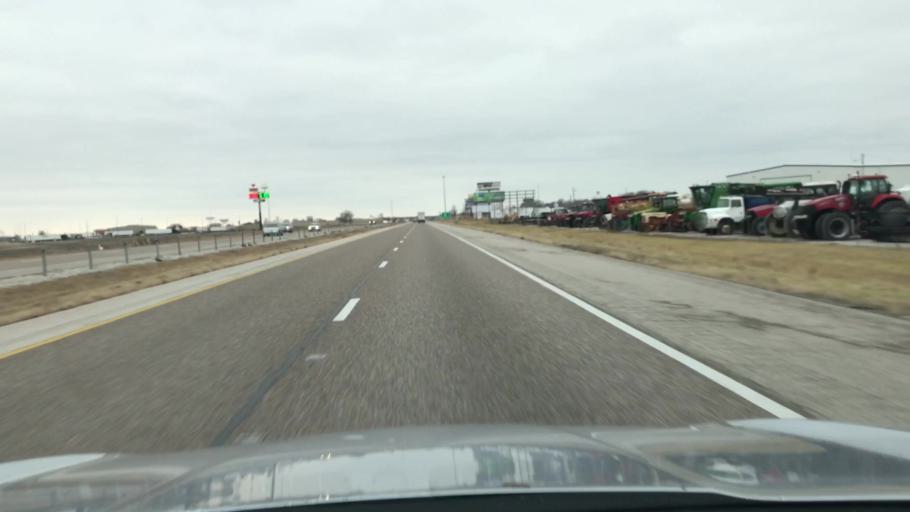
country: US
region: Illinois
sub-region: Madison County
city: Worden
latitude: 38.8969
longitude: -89.8332
